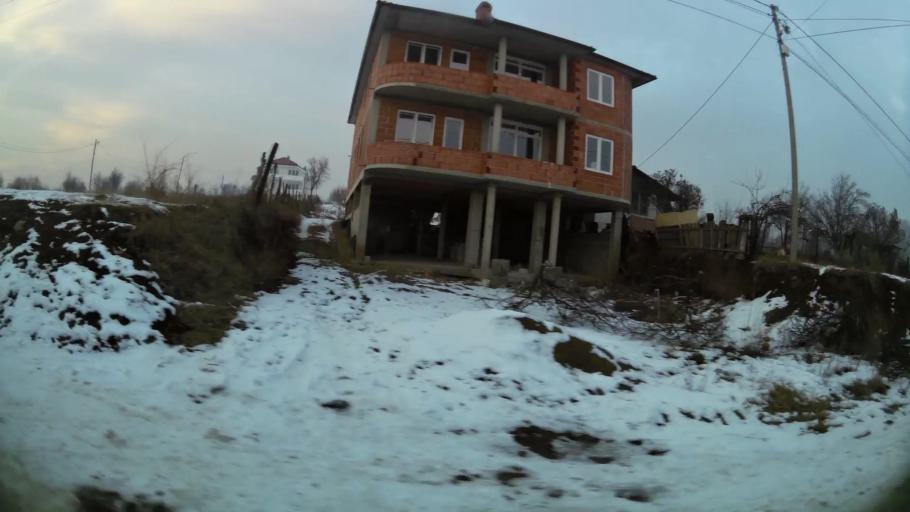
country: MK
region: Suto Orizari
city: Suto Orizare
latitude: 42.0394
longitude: 21.4043
